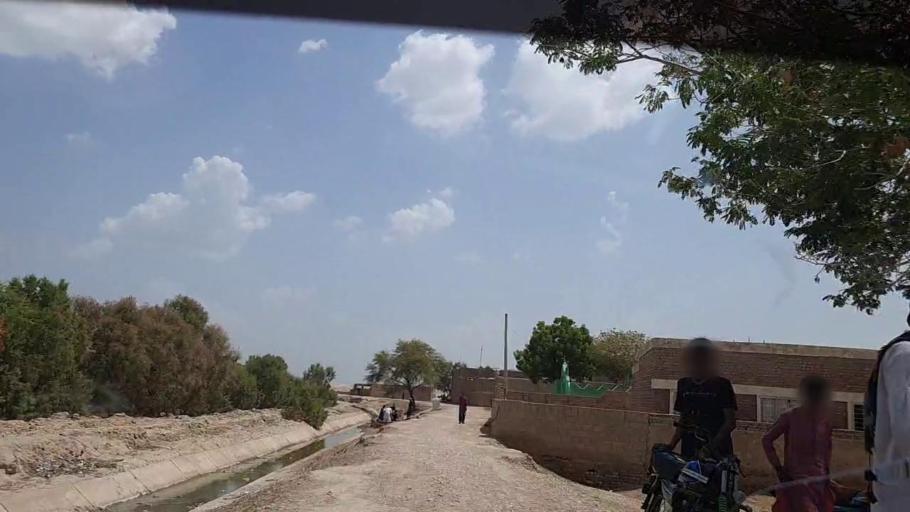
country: PK
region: Sindh
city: Bhan
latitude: 26.5049
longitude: 67.6394
